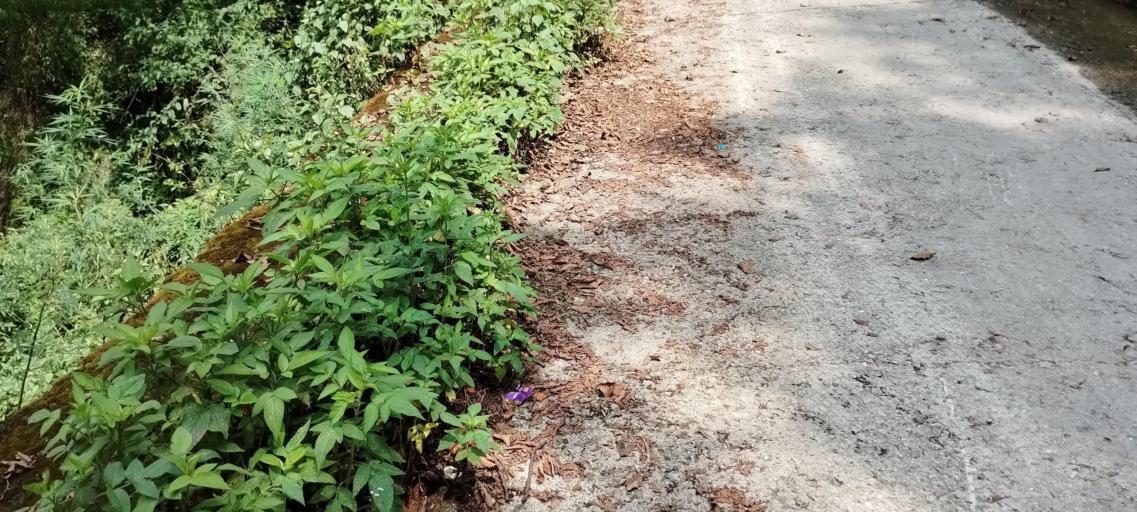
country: NP
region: Central Region
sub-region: Bagmati Zone
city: Kathmandu
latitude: 27.7909
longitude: 85.3598
